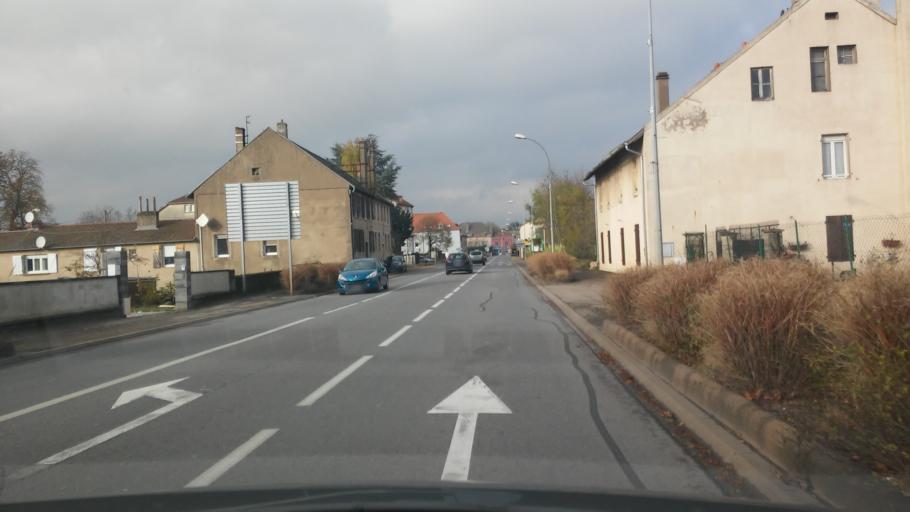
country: FR
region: Lorraine
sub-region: Departement de la Moselle
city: Uckange
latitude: 49.2984
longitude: 6.1641
